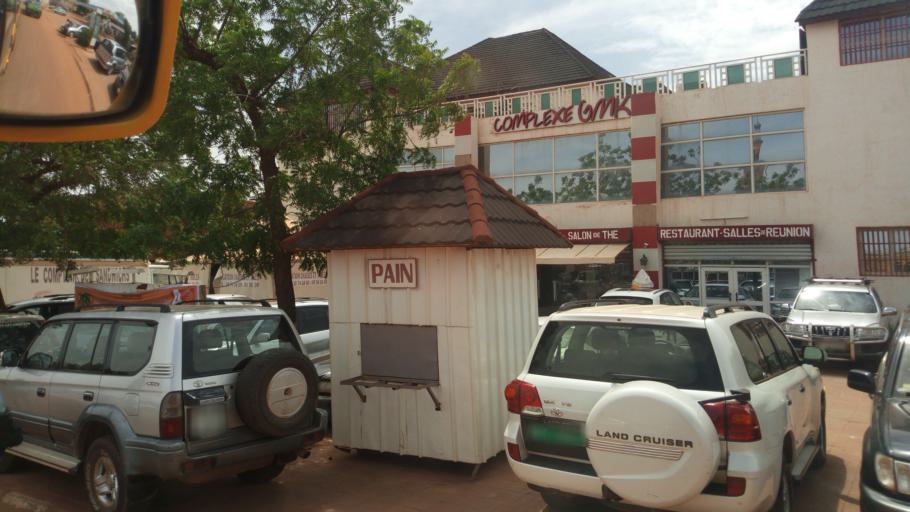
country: NE
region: Niamey
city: Niamey
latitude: 13.5205
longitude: 2.1341
